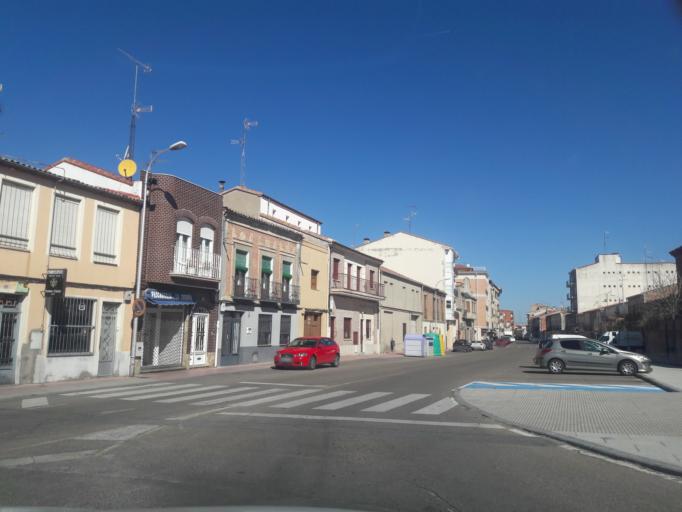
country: ES
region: Castille and Leon
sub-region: Provincia de Salamanca
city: Penaranda de Bracamonte
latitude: 40.8986
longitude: -5.2008
